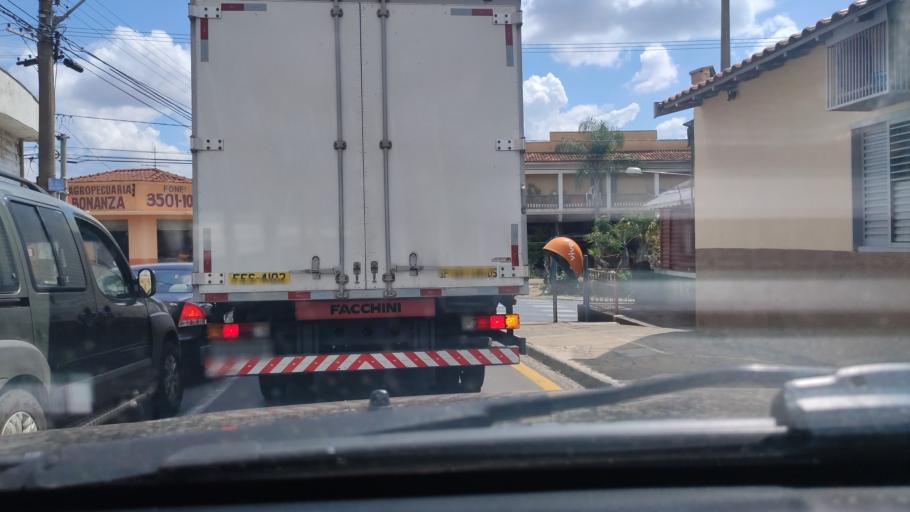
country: BR
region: Sao Paulo
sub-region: Sao Carlos
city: Sao Carlos
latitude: -22.0093
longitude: -47.8699
